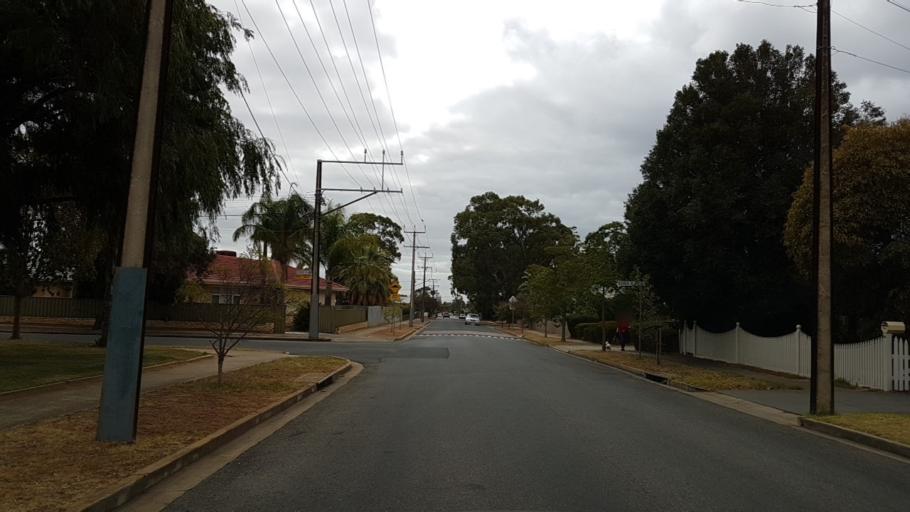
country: AU
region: South Australia
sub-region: Marion
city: Clovelly Park
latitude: -35.0021
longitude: 138.5696
